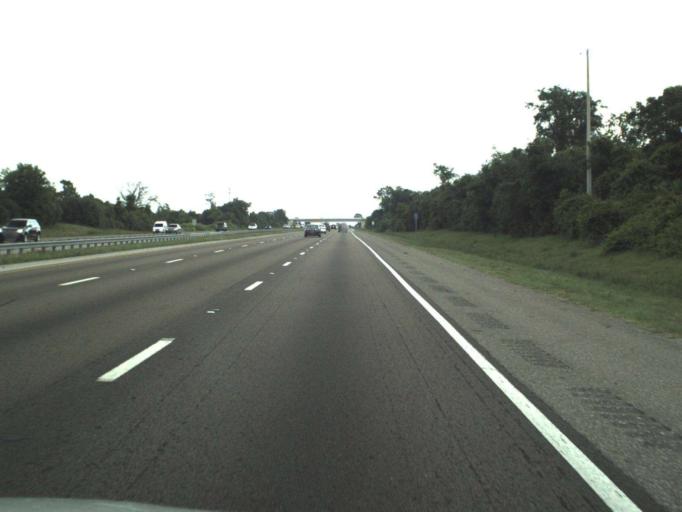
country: US
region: Florida
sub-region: Volusia County
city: Deltona
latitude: 28.8799
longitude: -81.2815
